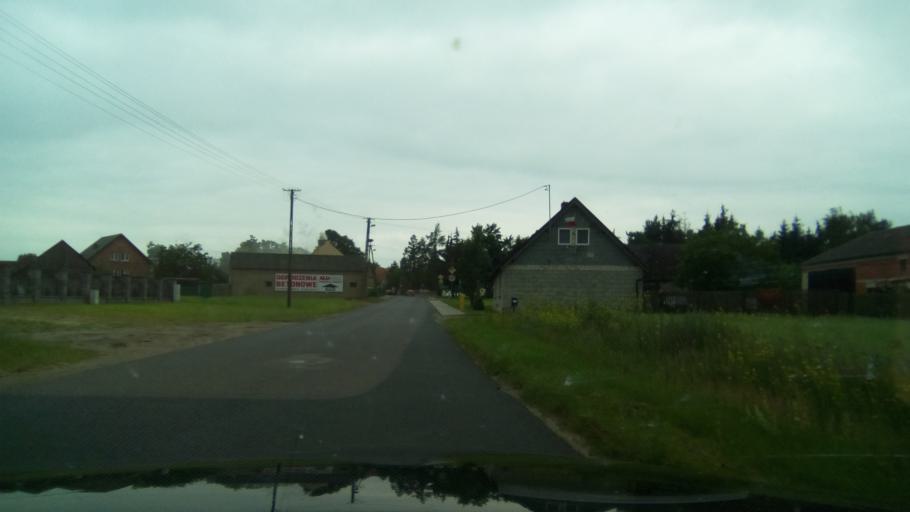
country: PL
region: Greater Poland Voivodeship
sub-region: Powiat gnieznienski
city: Czerniejewo
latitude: 52.4820
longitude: 17.5182
